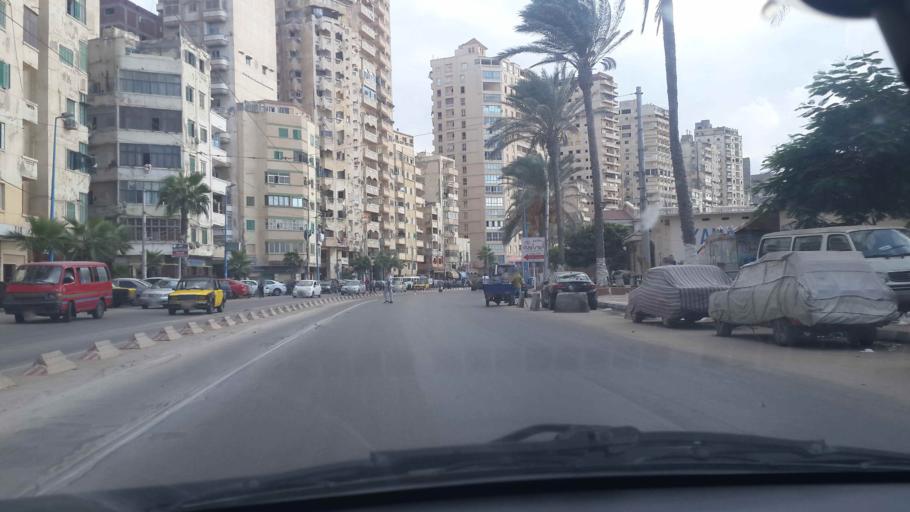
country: EG
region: Alexandria
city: Alexandria
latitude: 31.2068
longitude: 29.8789
